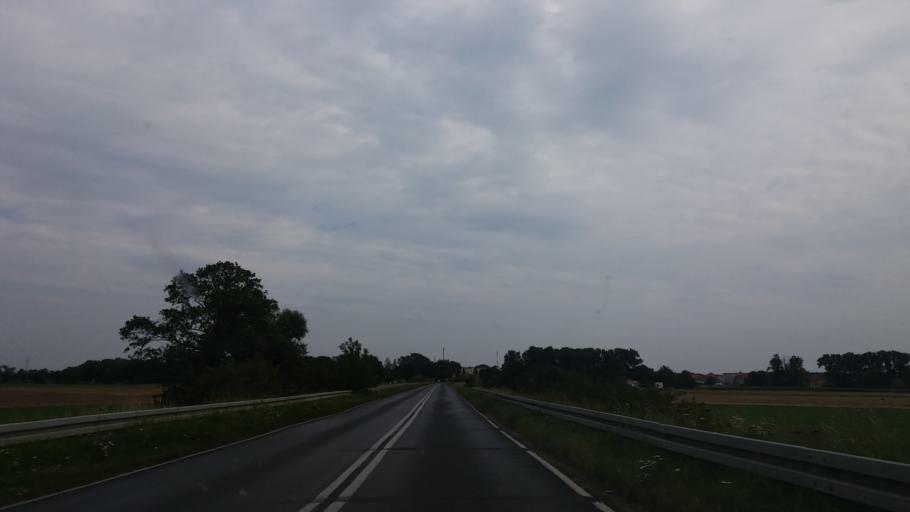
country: PL
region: Lubusz
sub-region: Powiat miedzyrzecki
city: Skwierzyna
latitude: 52.6041
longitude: 15.4887
